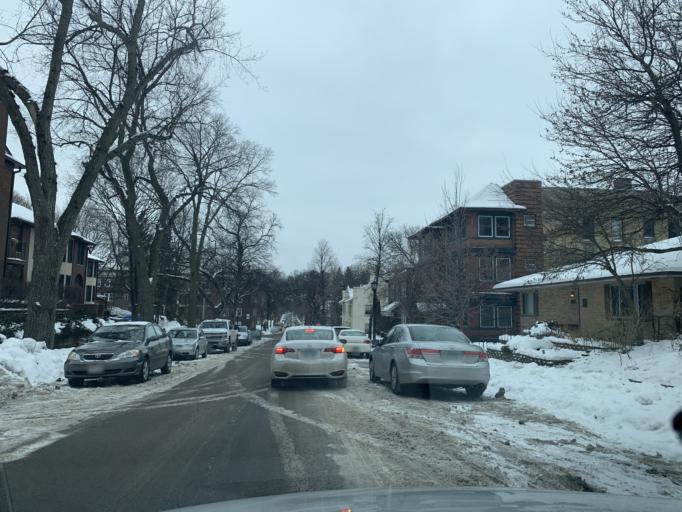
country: US
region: Minnesota
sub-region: Hennepin County
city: Minneapolis
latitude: 44.9638
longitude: -93.2944
